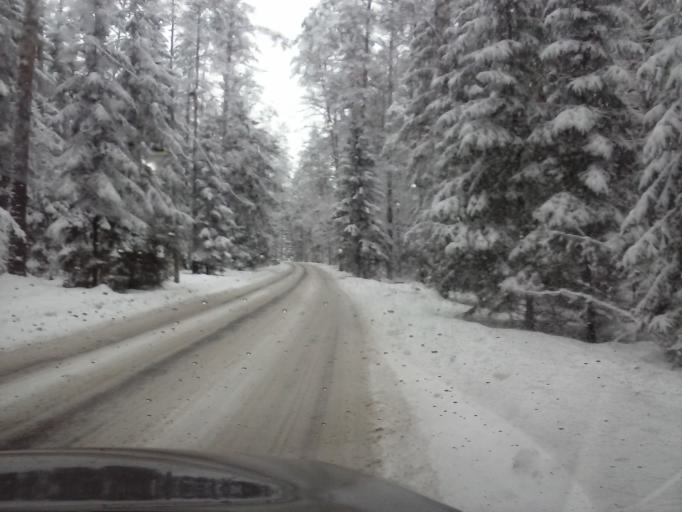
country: EE
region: Tartu
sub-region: Elva linn
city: Elva
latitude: 58.2153
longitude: 26.4254
